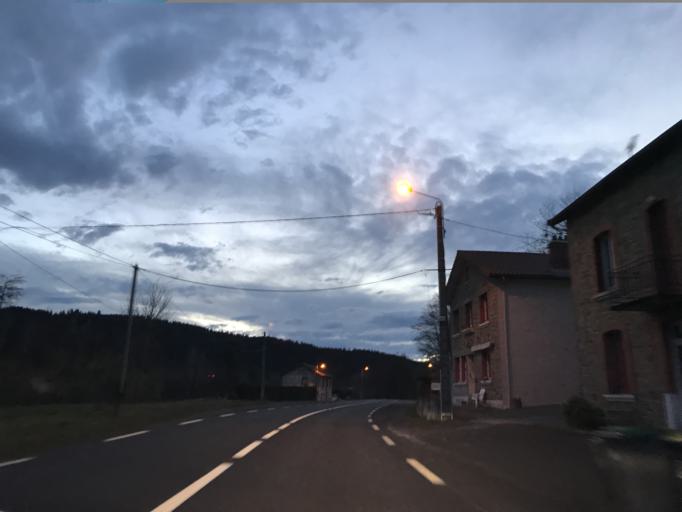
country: FR
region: Auvergne
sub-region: Departement du Puy-de-Dome
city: Chabreloche
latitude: 45.8767
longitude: 3.6803
